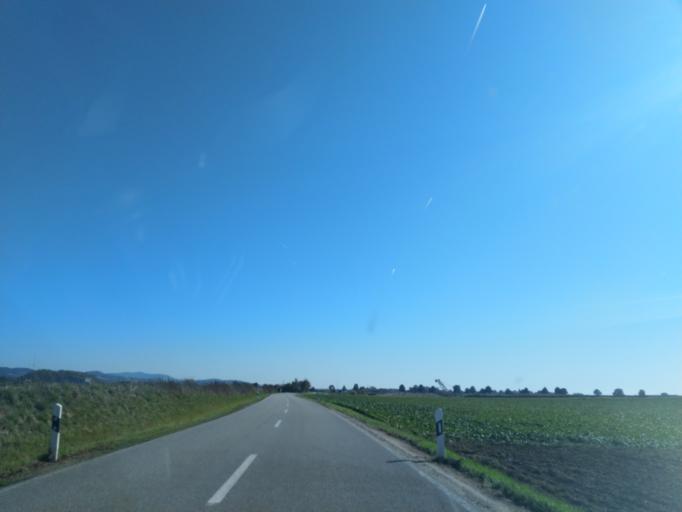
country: DE
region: Bavaria
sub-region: Lower Bavaria
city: Offenberg
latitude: 48.8224
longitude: 12.8704
